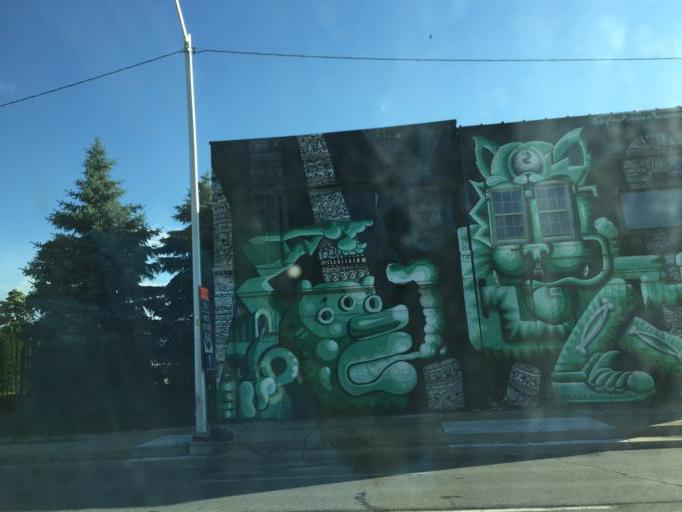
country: US
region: Michigan
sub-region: Wayne County
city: Detroit
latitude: 42.3447
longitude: -83.0792
